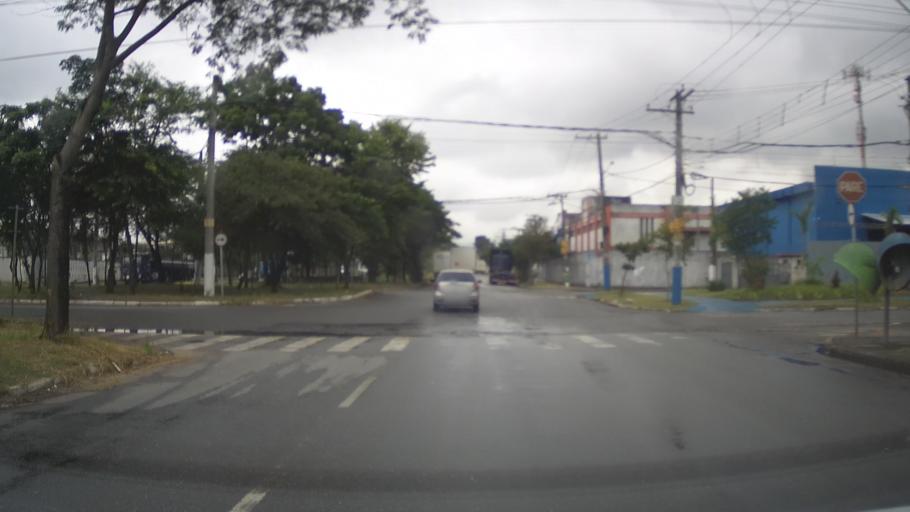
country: BR
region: Sao Paulo
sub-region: Guarulhos
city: Guarulhos
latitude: -23.4685
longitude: -46.4687
